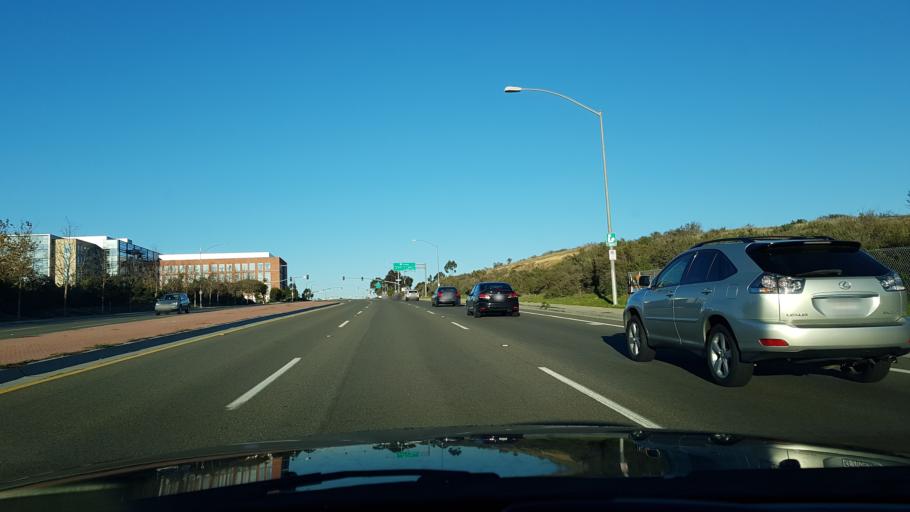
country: US
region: California
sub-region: San Diego County
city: La Jolla
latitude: 32.8658
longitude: -117.1987
